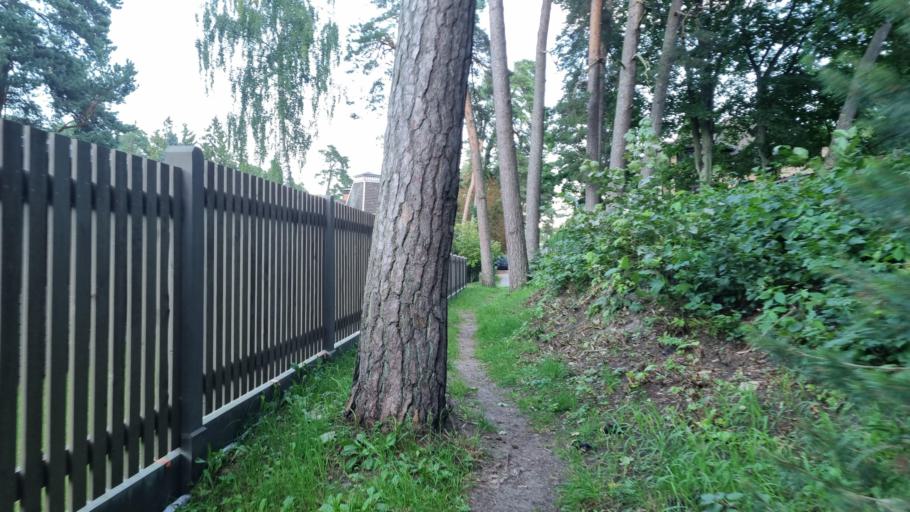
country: LV
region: Jurmala
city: Jurmala
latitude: 56.9648
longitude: 23.7322
